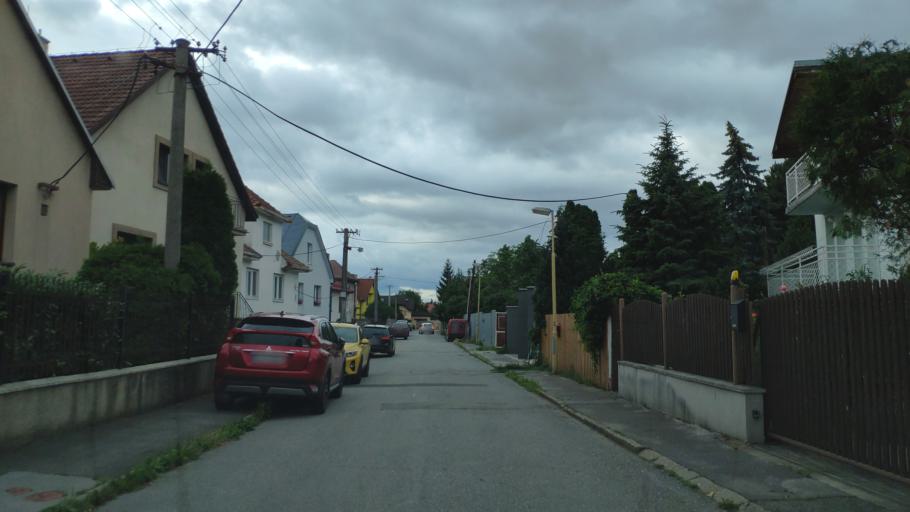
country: SK
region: Kosicky
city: Kosice
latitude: 48.7207
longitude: 21.2788
